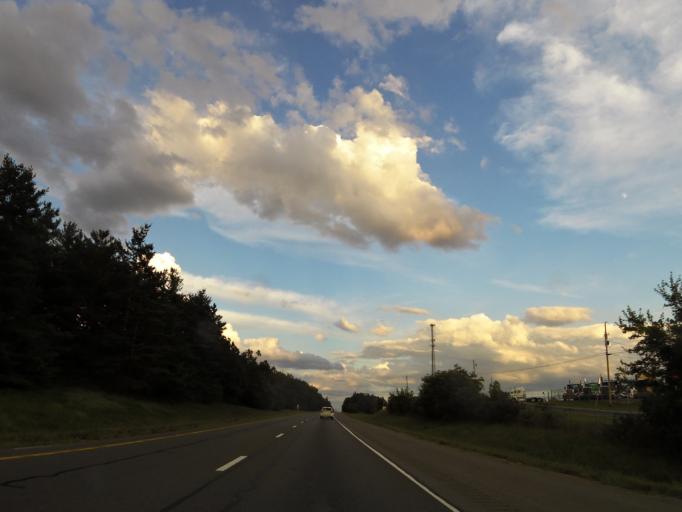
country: US
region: Tennessee
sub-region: Cumberland County
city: Crossville
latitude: 36.0477
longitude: -85.1399
